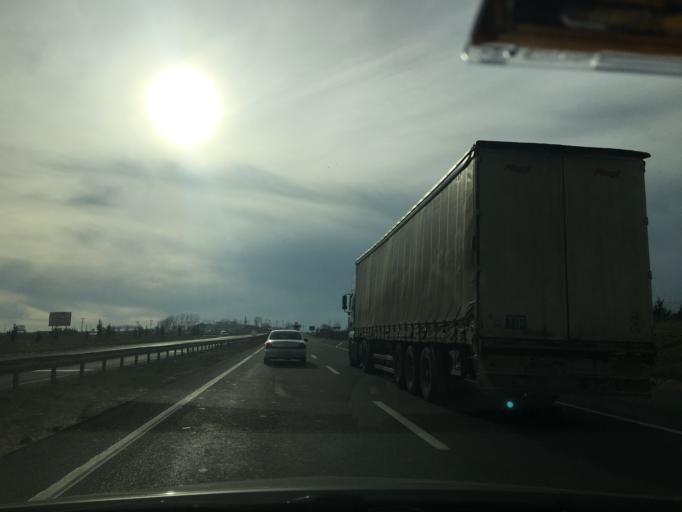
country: TR
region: Istanbul
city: Buyukcavuslu
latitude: 41.2300
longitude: 28.0580
